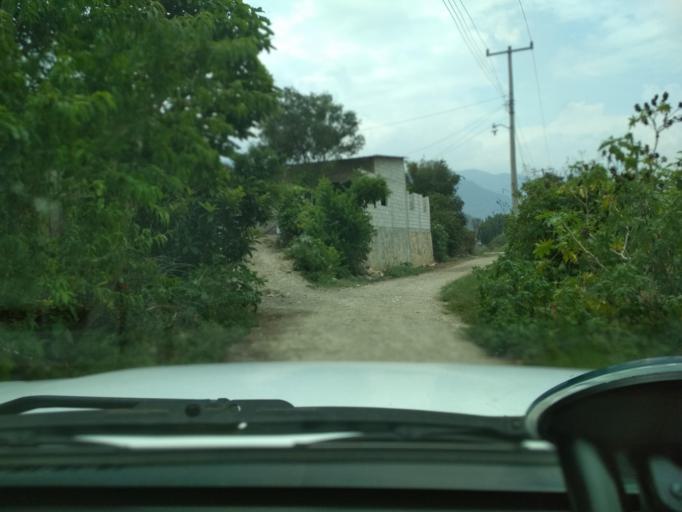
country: MX
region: Veracruz
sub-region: Nogales
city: Taza de Agua Ojo Zarco
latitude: 18.7738
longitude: -97.2092
